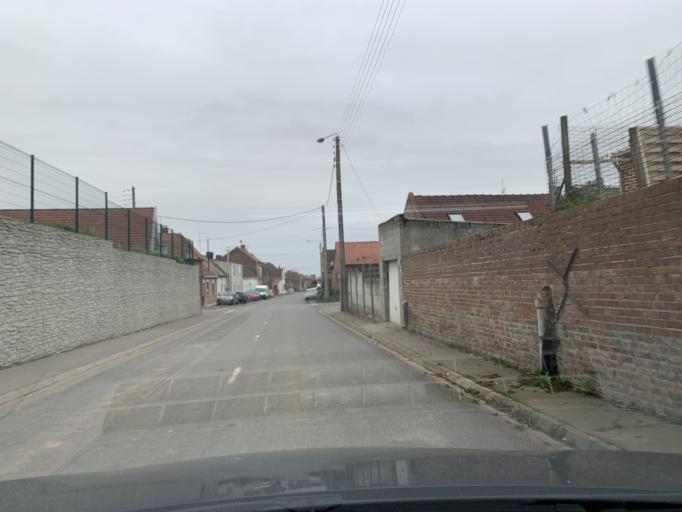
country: FR
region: Nord-Pas-de-Calais
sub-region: Departement du Pas-de-Calais
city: Oisy-le-Verger
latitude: 50.2506
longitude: 3.1261
